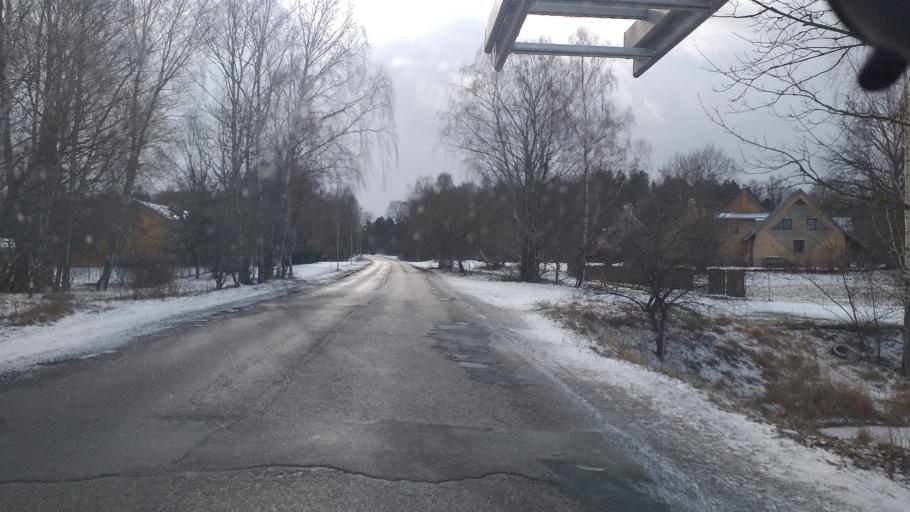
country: LV
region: Riga
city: Bolderaja
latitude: 56.9868
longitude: 24.0319
